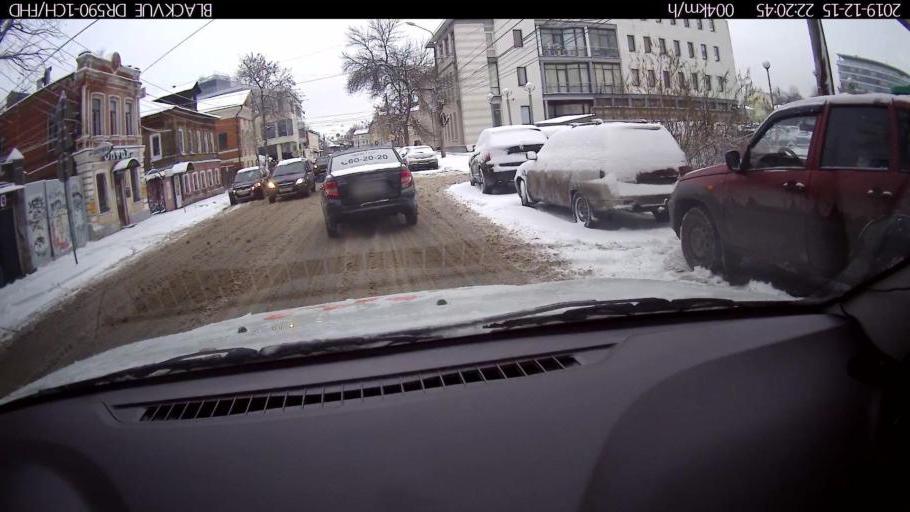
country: RU
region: Nizjnij Novgorod
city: Nizhniy Novgorod
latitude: 56.3217
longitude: 44.0085
